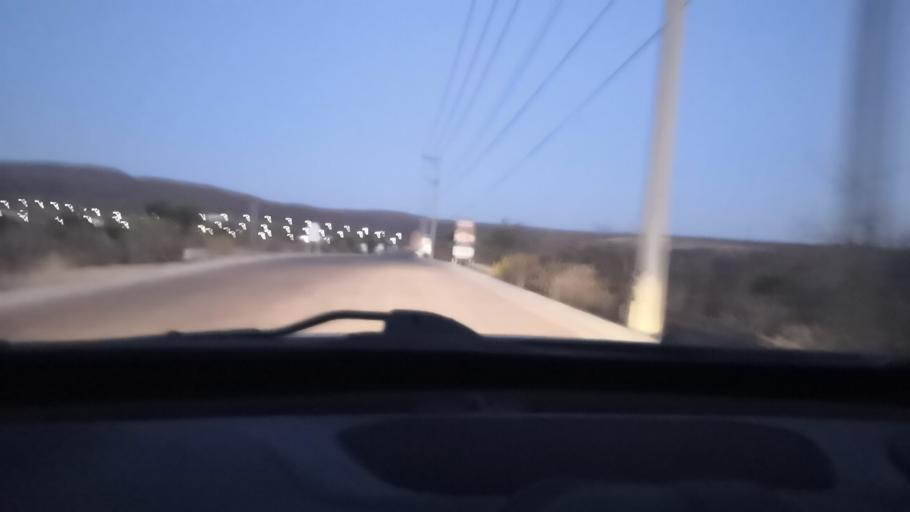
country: MX
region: Guanajuato
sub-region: Leon
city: Fraccionamiento Paseo de las Torres
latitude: 21.2359
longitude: -101.7909
